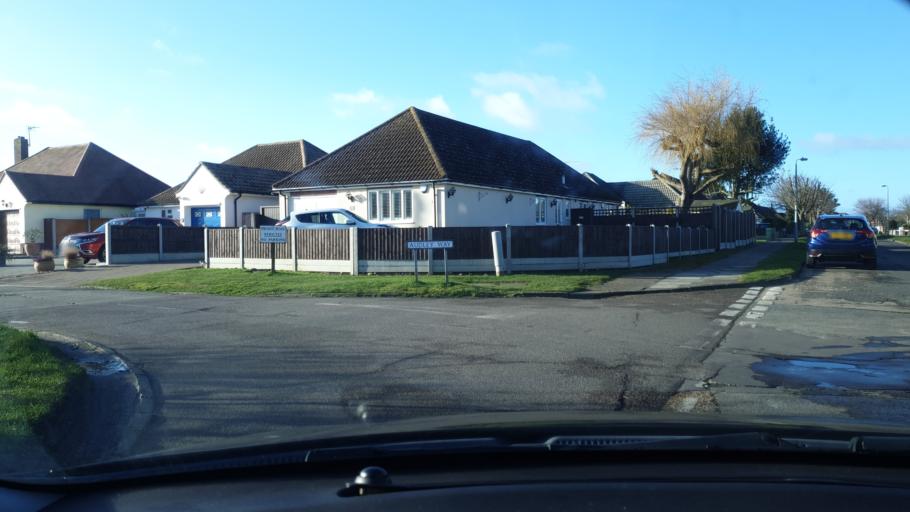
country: GB
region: England
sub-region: Essex
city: Walton-on-the-Naze
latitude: 51.8398
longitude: 1.2569
